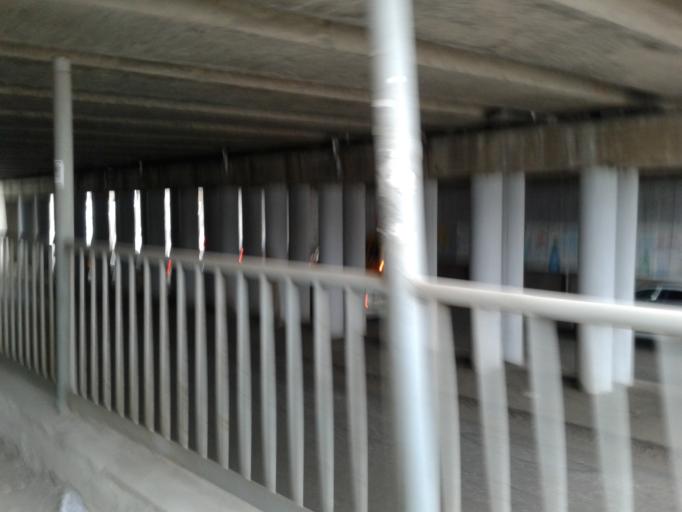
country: RU
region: Volgograd
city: Volgograd
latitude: 48.7241
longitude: 44.5285
